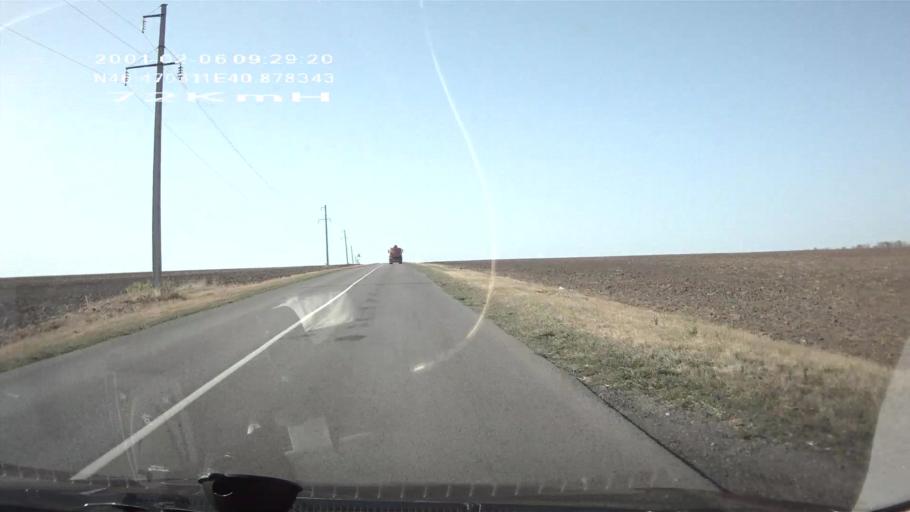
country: RU
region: Rostov
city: Tselina
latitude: 46.4700
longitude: 40.8779
